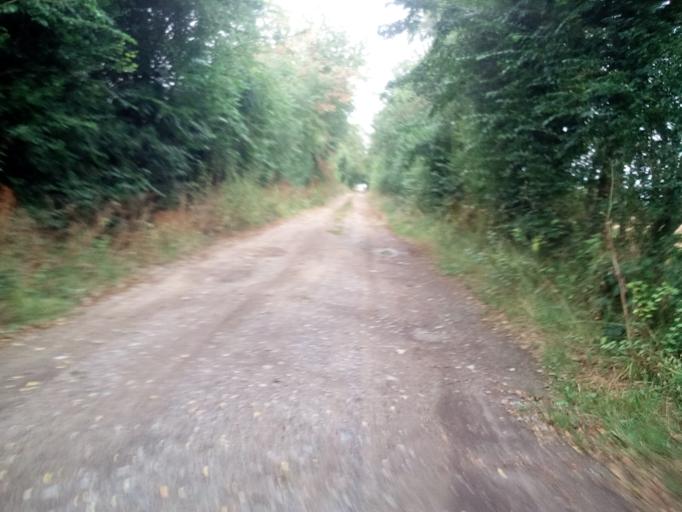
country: FR
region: Lower Normandy
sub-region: Departement du Calvados
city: Clinchamps-sur-Orne
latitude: 49.0421
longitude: -0.3993
